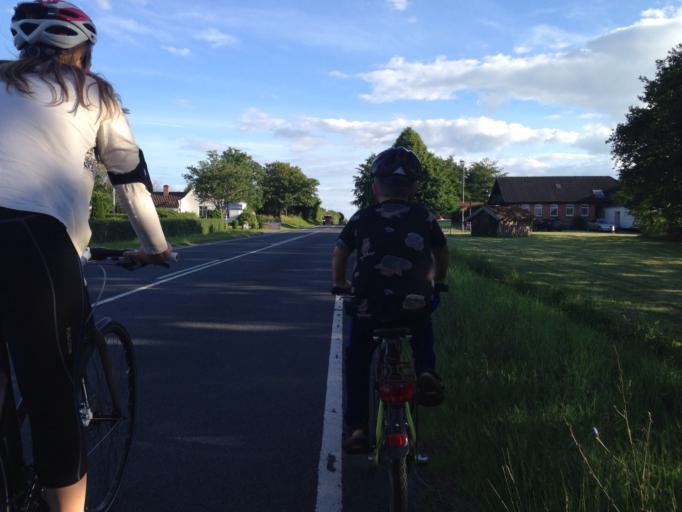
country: DK
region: South Denmark
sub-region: Middelfart Kommune
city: Norre Aby
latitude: 55.4822
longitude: 9.9018
